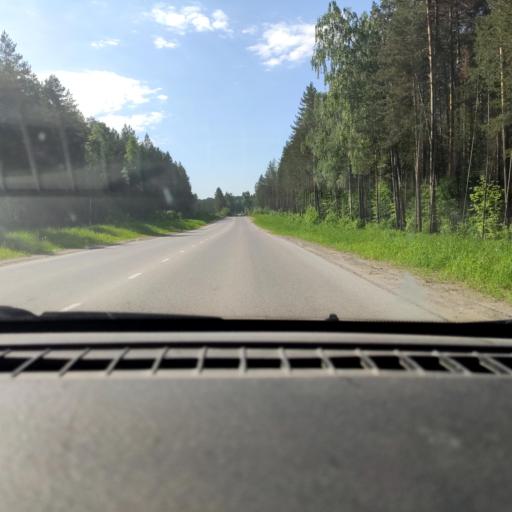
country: RU
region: Perm
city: Overyata
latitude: 58.0007
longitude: 55.8793
